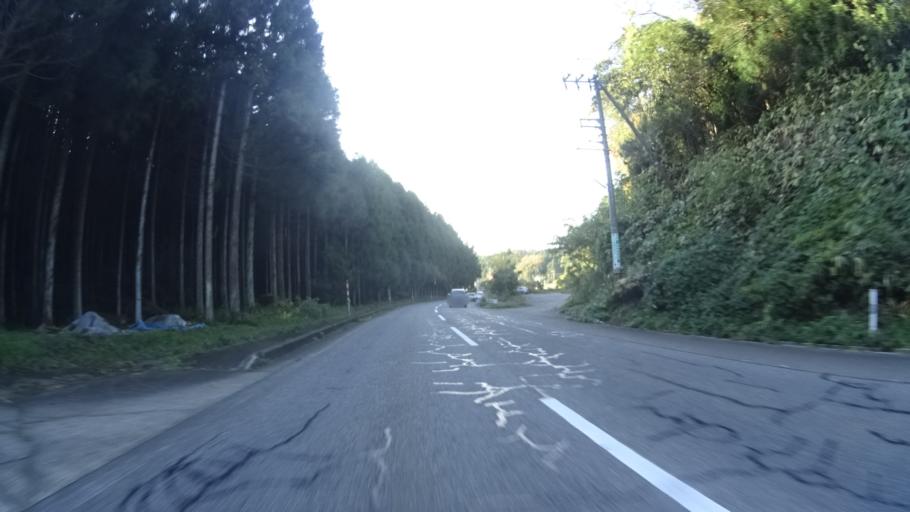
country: JP
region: Ishikawa
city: Hakui
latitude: 37.0061
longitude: 136.8021
